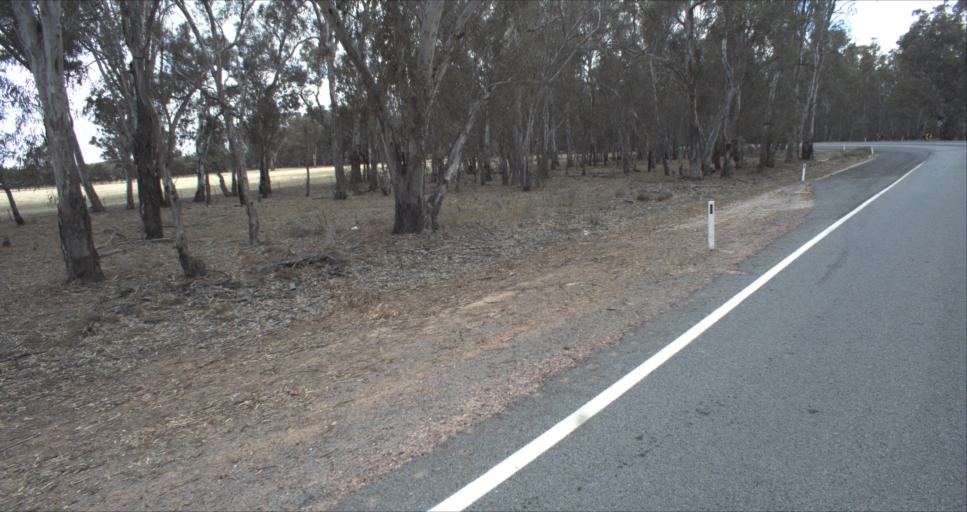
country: AU
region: New South Wales
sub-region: Leeton
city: Leeton
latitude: -34.6309
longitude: 146.3754
